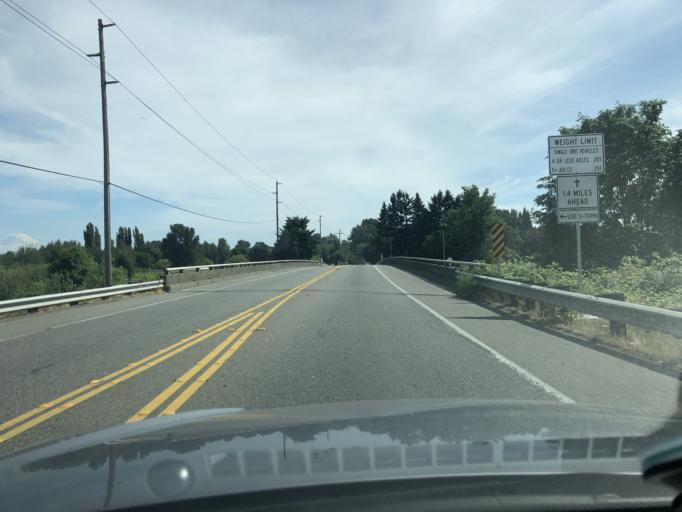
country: US
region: Washington
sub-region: King County
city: Kent
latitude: 47.3767
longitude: -122.2473
